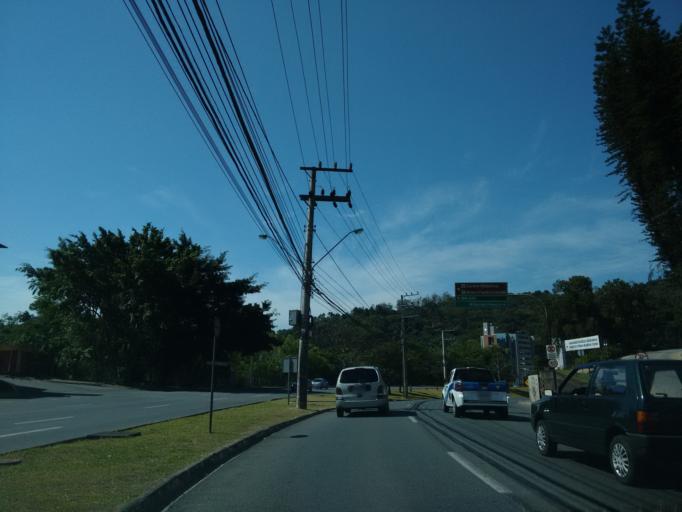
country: BR
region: Santa Catarina
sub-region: Blumenau
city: Blumenau
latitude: -26.9253
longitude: -49.0563
